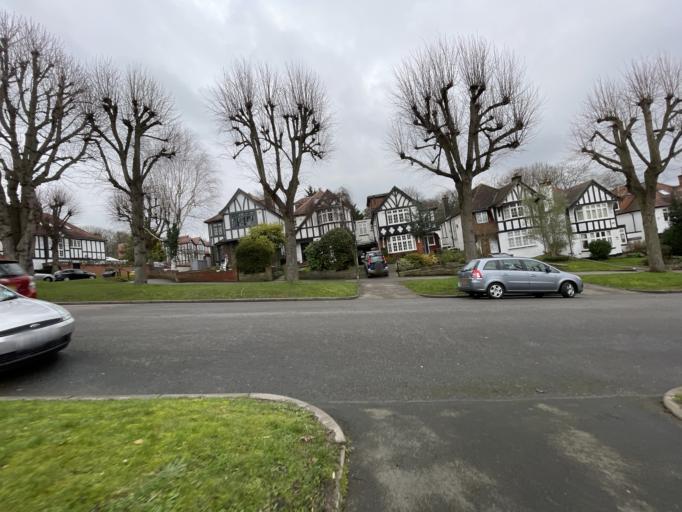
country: GB
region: England
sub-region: Greater London
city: Camden Town
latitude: 51.5653
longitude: -0.1498
